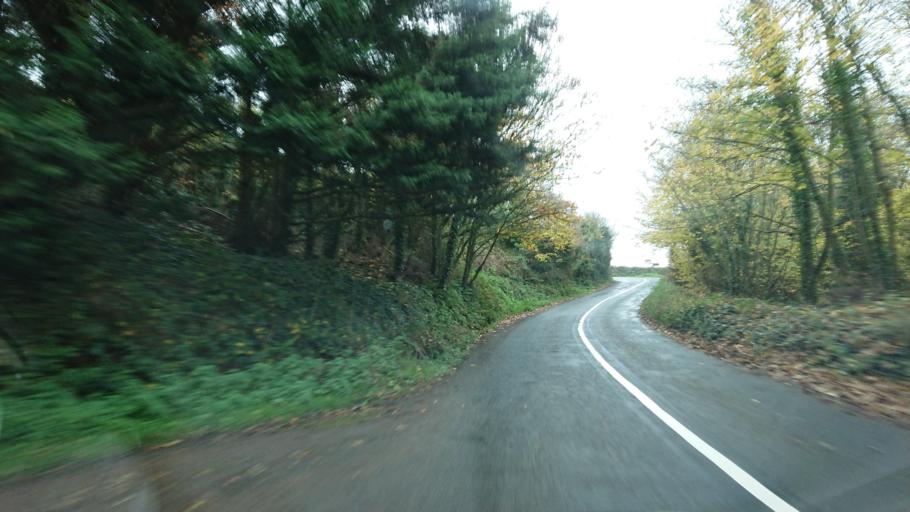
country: IE
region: Munster
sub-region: Waterford
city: Dunmore East
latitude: 52.1605
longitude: -7.0622
